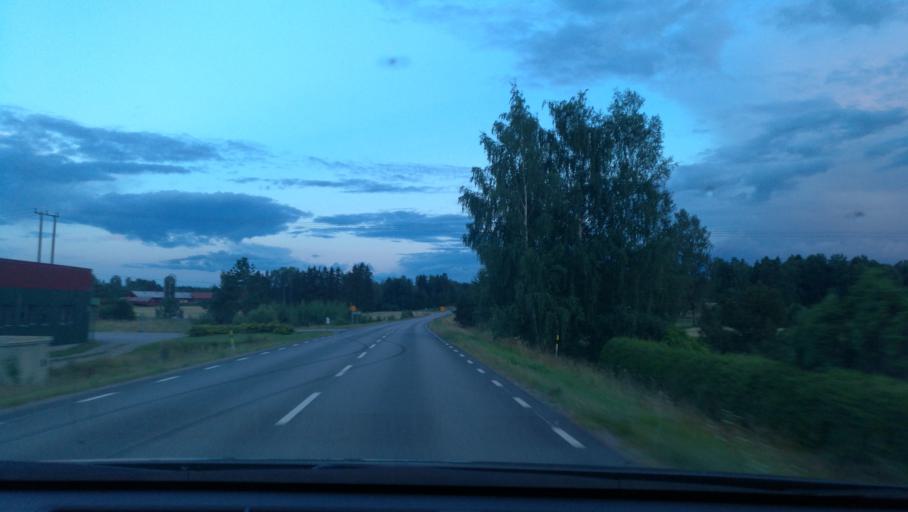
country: SE
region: OEstergoetland
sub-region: Norrkopings Kommun
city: Svartinge
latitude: 58.8232
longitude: 15.9422
